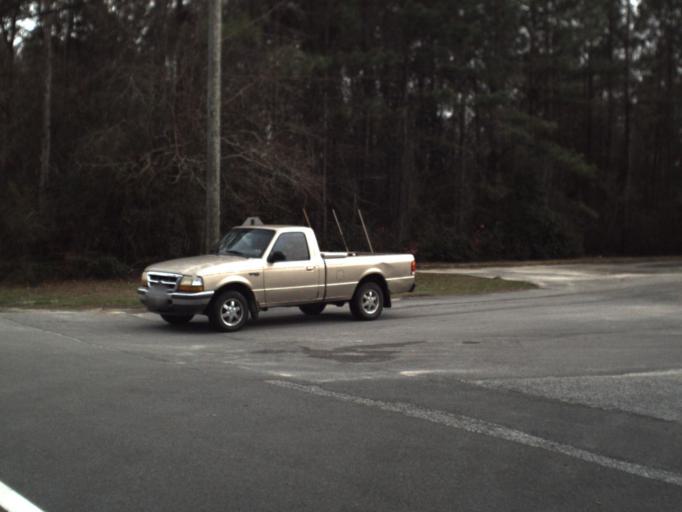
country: US
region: Florida
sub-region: Gulf County
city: Wewahitchka
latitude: 30.1150
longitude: -85.2049
